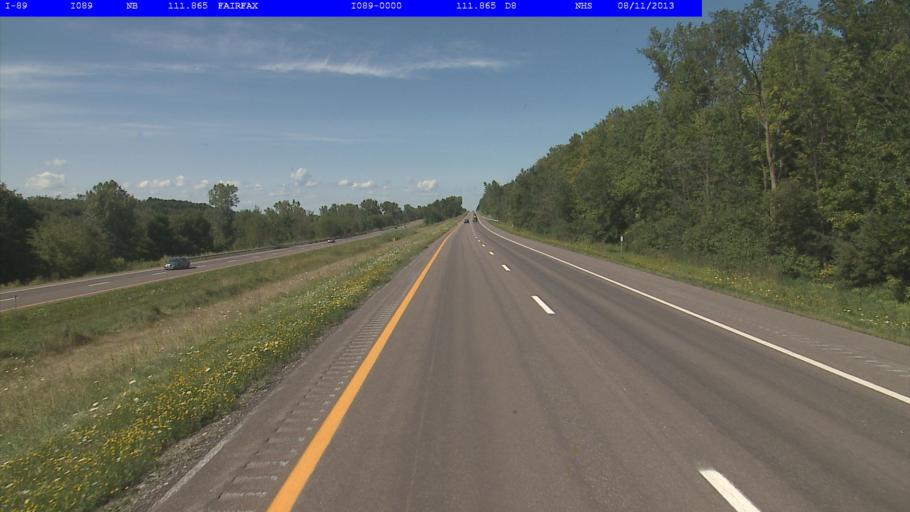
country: US
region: Vermont
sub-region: Franklin County
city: Saint Albans
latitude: 44.7681
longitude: -73.0756
